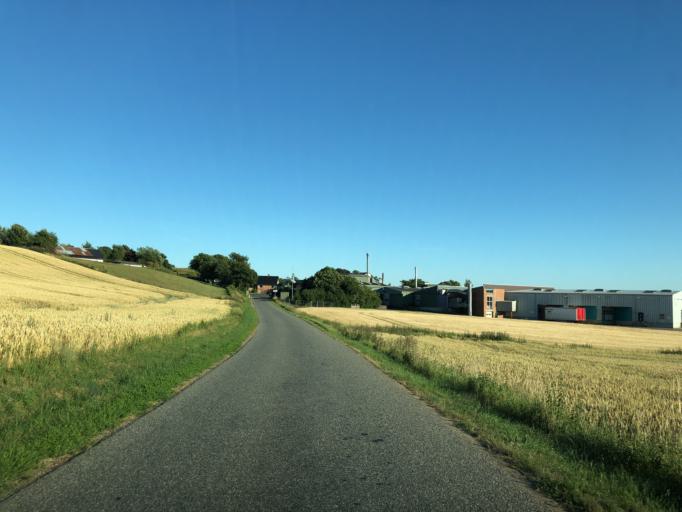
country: DK
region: Central Jutland
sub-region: Skanderborg Kommune
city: Ry
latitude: 55.9894
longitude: 9.7871
